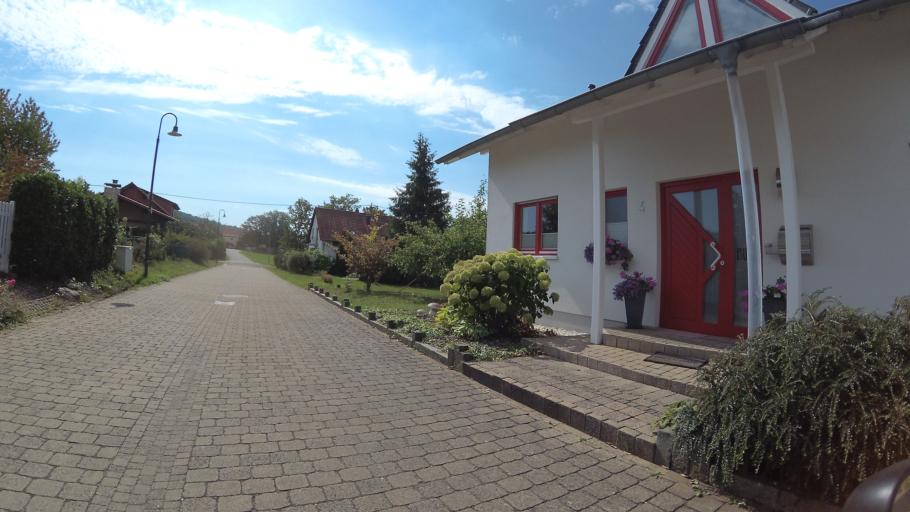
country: DE
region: Saarland
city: Gersheim
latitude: 49.1353
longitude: 7.2051
